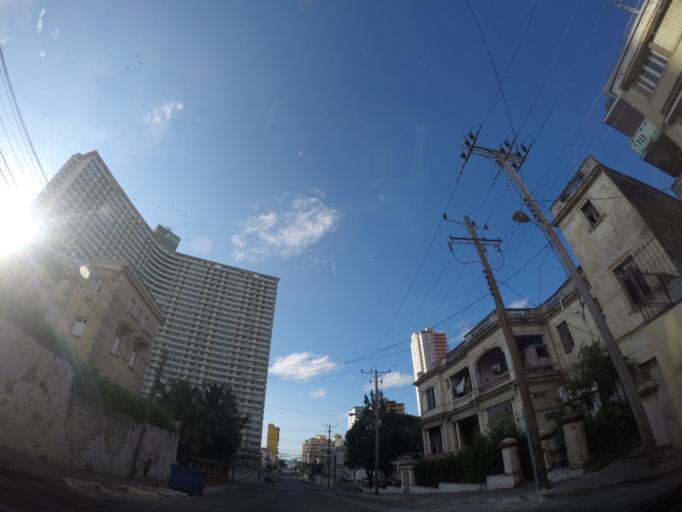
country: CU
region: La Habana
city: Havana
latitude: 23.1424
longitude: -82.3830
